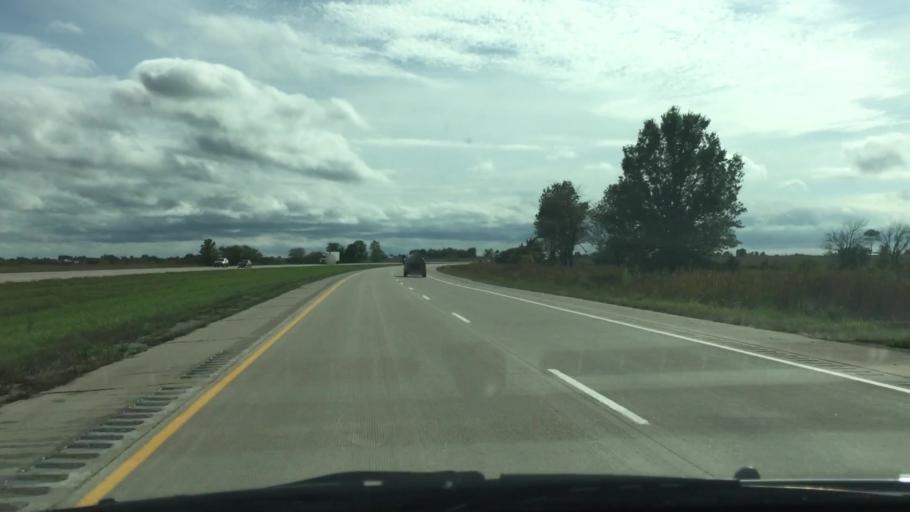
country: US
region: Iowa
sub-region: Decatur County
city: Leon
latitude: 40.8463
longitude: -93.8044
